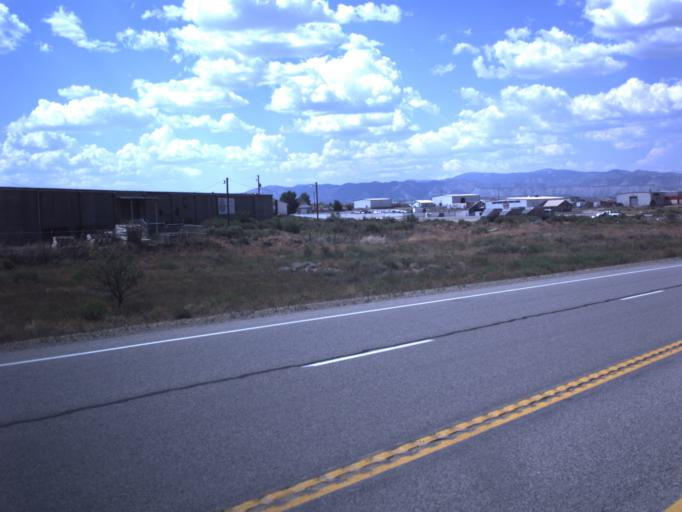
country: US
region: Utah
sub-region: Carbon County
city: Price
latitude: 39.5480
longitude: -110.8156
